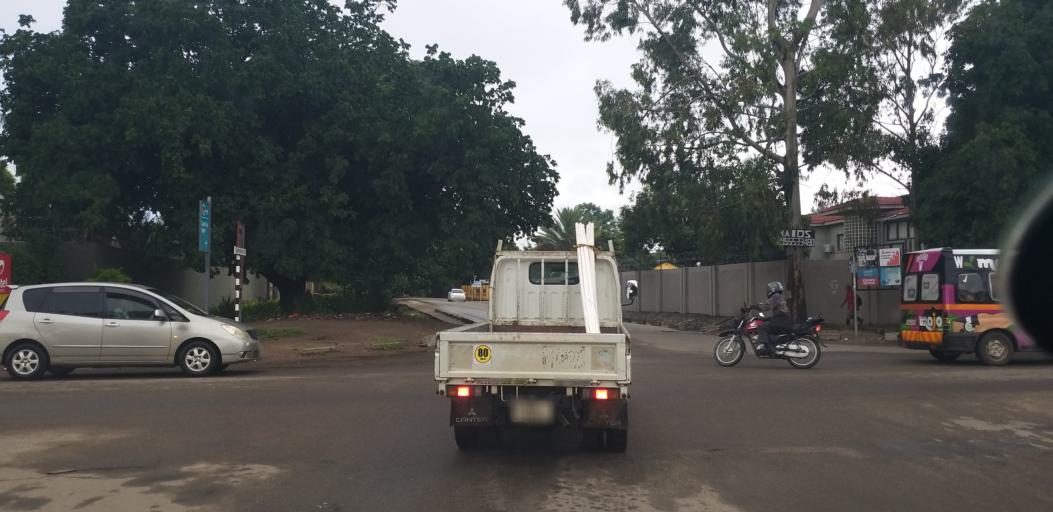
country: ZM
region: Lusaka
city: Lusaka
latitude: -15.4212
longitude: 28.2939
